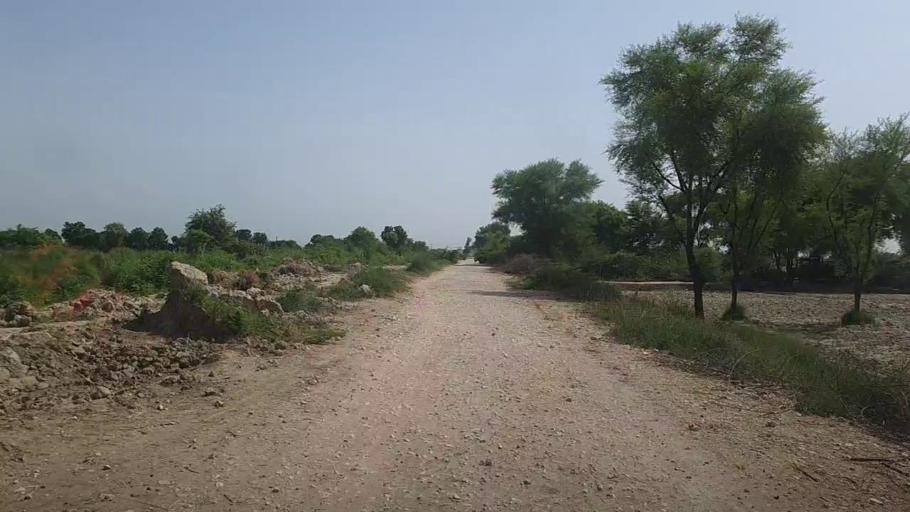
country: PK
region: Sindh
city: Pad Idan
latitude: 26.7866
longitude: 68.3255
